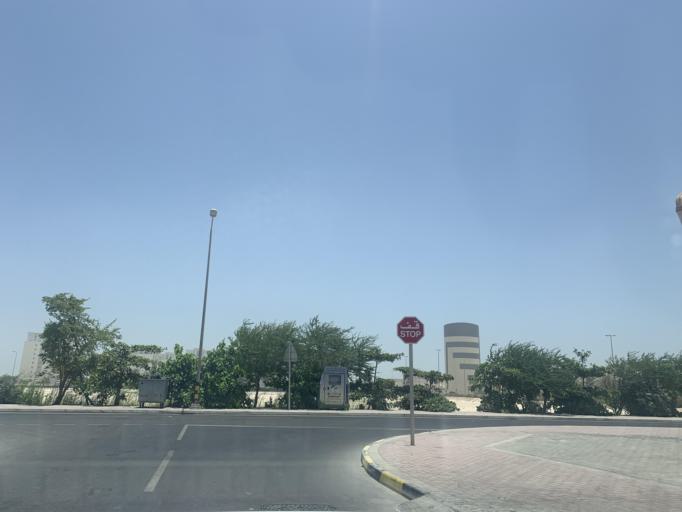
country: BH
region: Manama
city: Jidd Hafs
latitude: 26.2351
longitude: 50.4590
